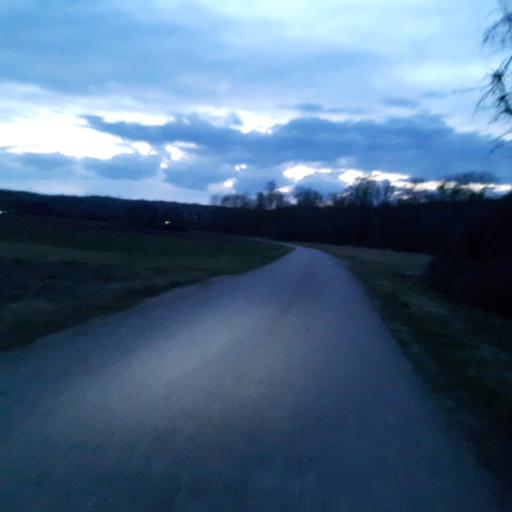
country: DE
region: Baden-Wuerttemberg
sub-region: Regierungsbezirk Stuttgart
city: Walheim
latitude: 49.0051
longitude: 9.1640
